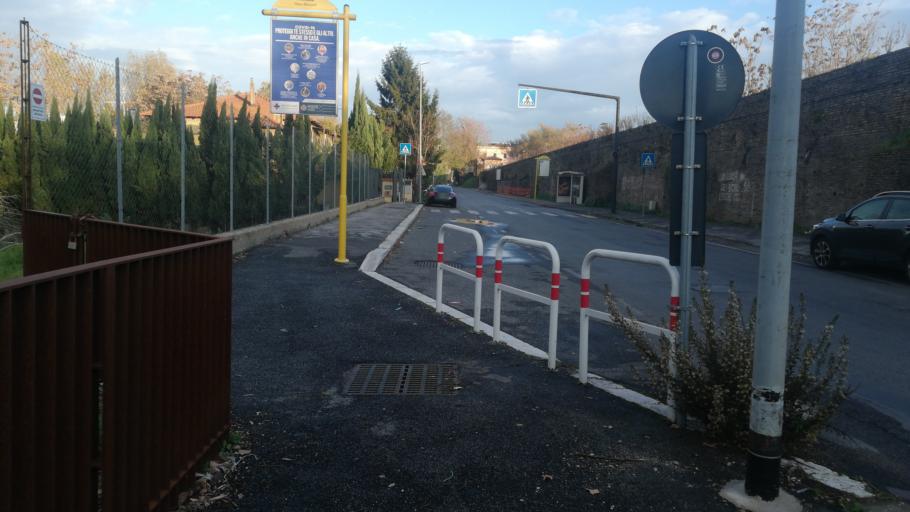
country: IT
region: Latium
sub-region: Citta metropolitana di Roma Capitale
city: Rome
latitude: 41.9269
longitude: 12.5305
